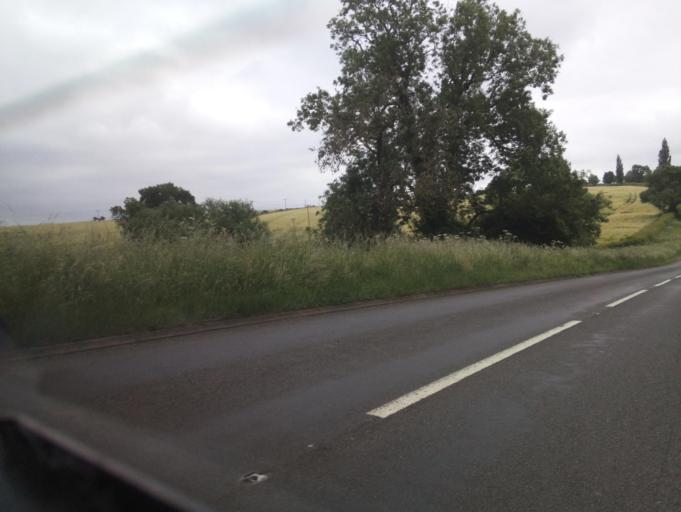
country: GB
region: England
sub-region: District of Rutland
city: Preston
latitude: 52.6046
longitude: -0.7199
